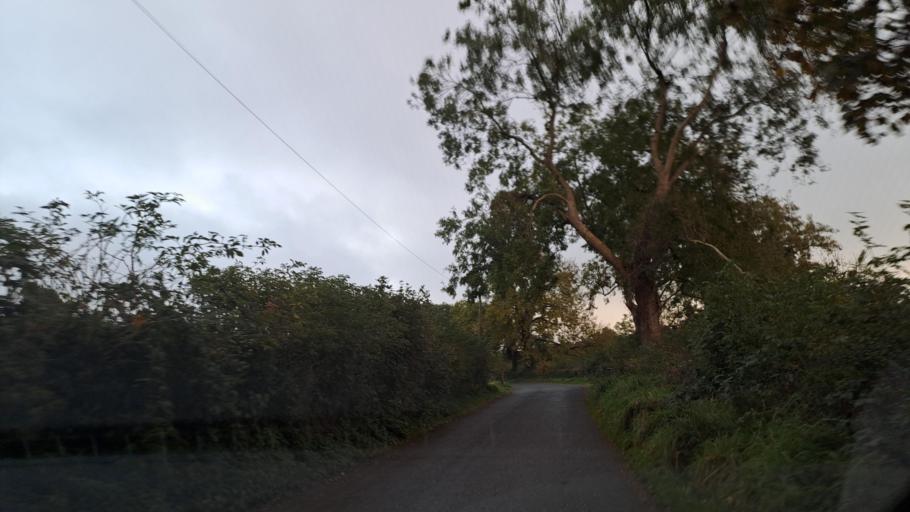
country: IE
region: Ulster
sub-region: County Monaghan
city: Carrickmacross
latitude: 53.9828
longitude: -6.6857
